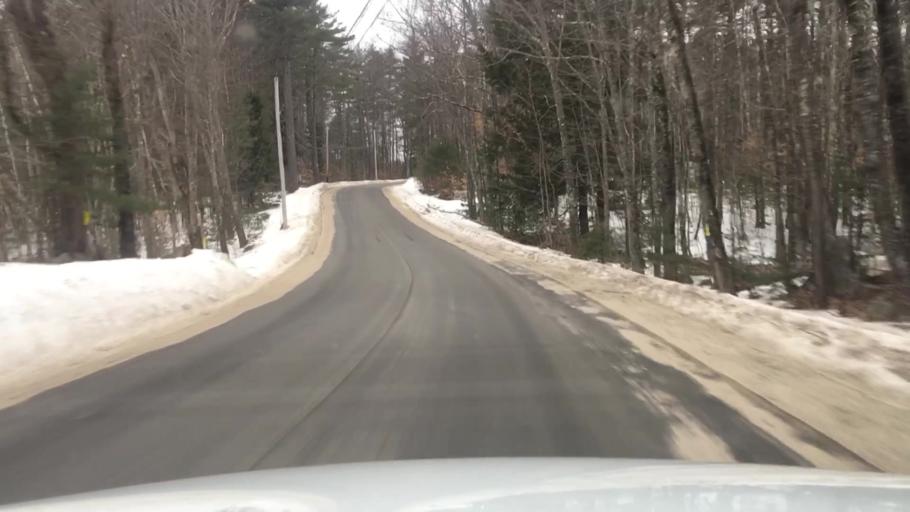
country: US
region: Maine
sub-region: York County
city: Shapleigh
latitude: 43.5252
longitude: -70.8432
